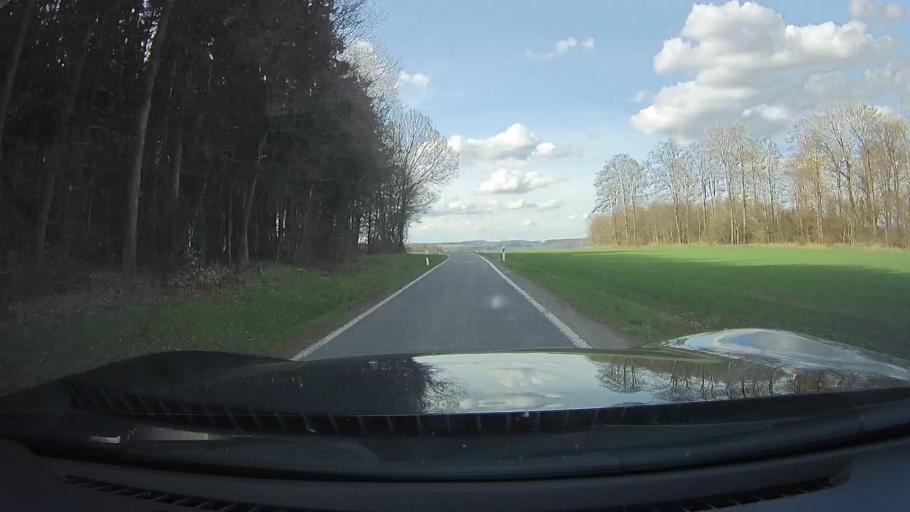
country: DE
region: Bavaria
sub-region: Regierungsbezirk Unterfranken
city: Weilbach
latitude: 49.6196
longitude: 9.2728
